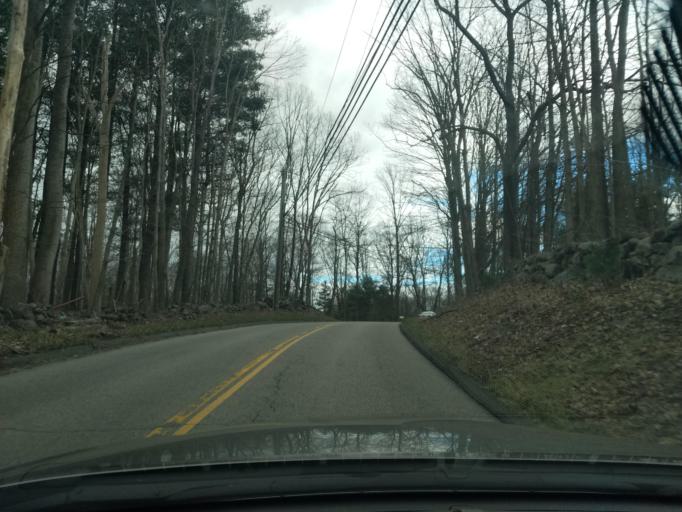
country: US
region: Connecticut
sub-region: Fairfield County
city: Newtown
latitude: 41.3681
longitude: -73.3310
